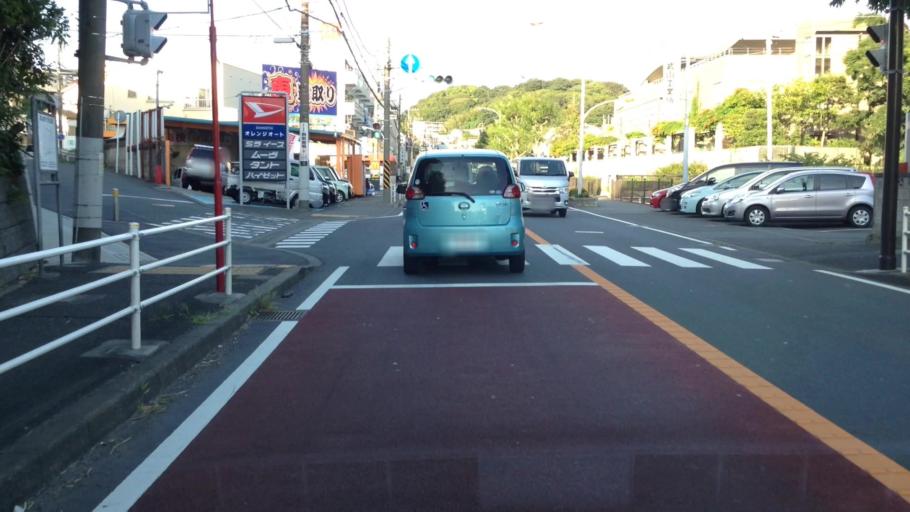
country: JP
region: Kanagawa
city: Yokosuka
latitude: 35.2245
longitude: 139.6437
